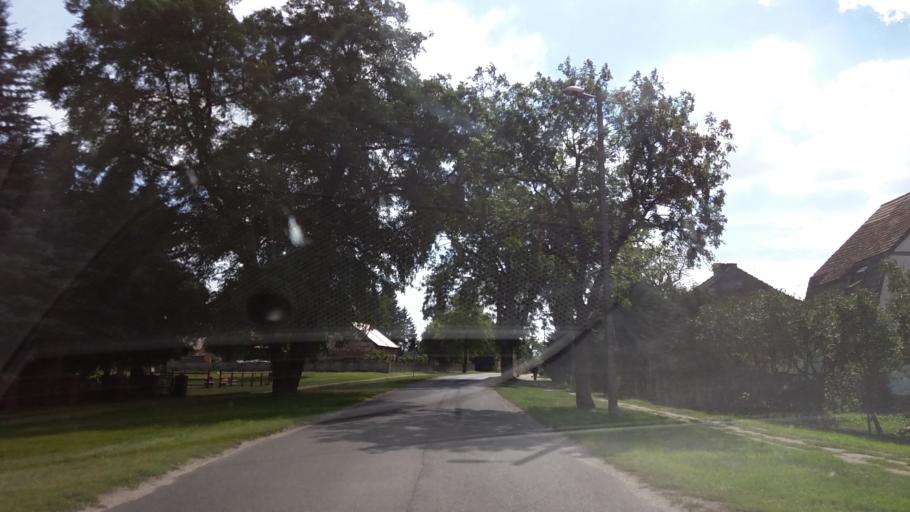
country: PL
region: West Pomeranian Voivodeship
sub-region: Powiat stargardzki
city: Kobylanka
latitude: 53.3672
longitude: 14.8612
